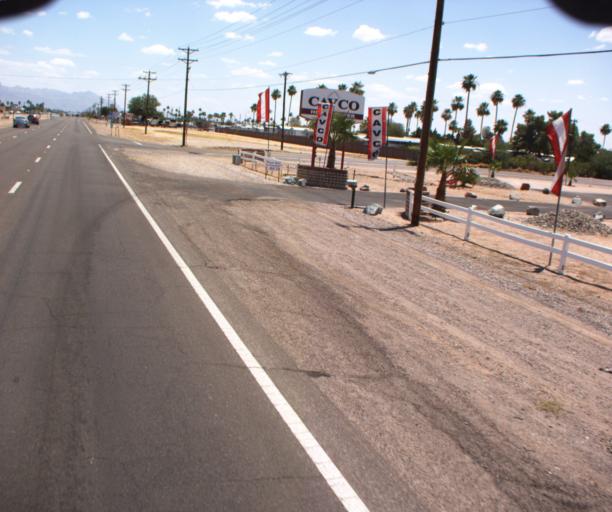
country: US
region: Arizona
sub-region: Pinal County
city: Apache Junction
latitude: 33.4151
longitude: -111.6508
